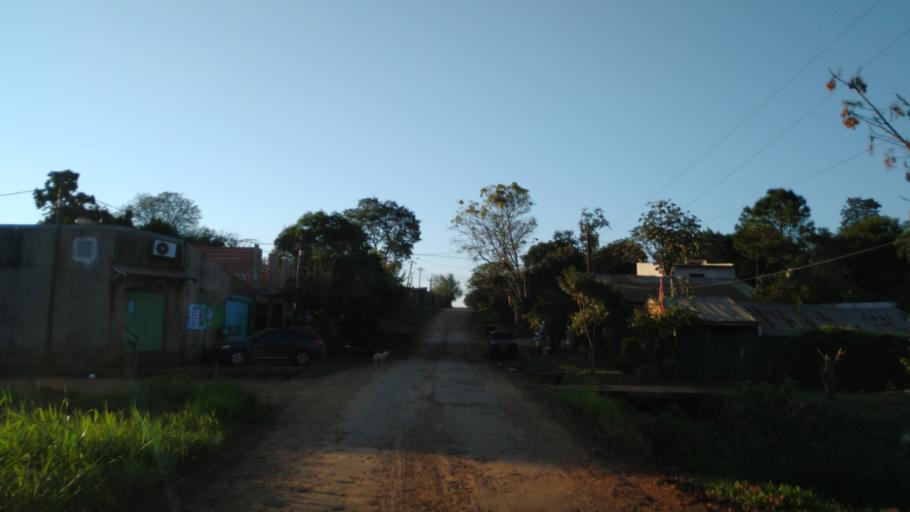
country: AR
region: Misiones
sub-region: Departamento de Capital
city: Posadas
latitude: -27.4211
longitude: -55.9204
